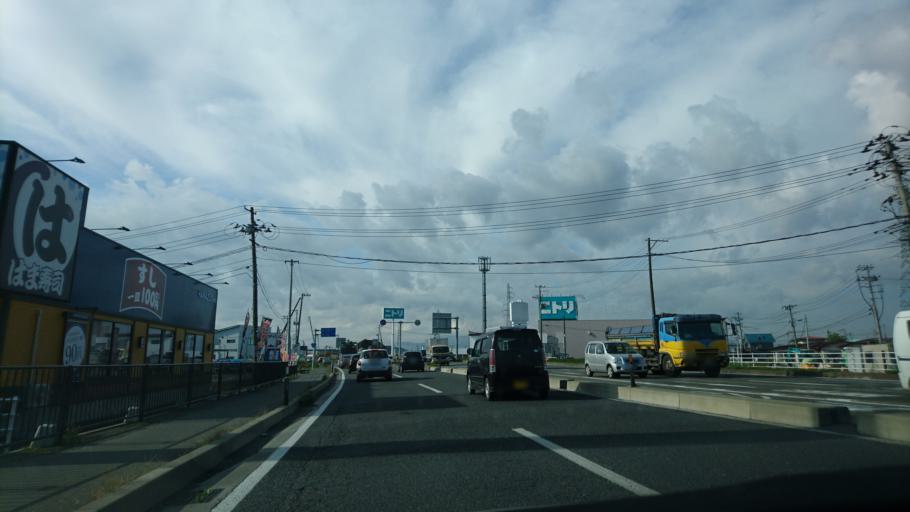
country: JP
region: Miyagi
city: Furukawa
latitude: 38.5841
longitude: 140.9480
